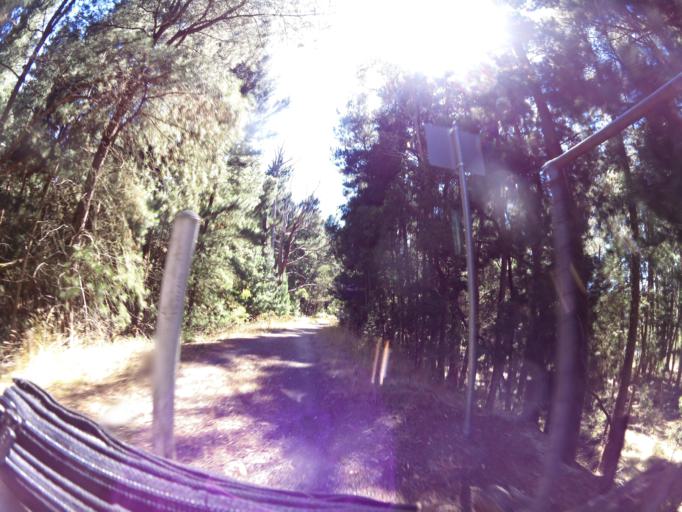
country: AU
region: Victoria
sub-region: Ballarat North
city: Delacombe
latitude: -37.6795
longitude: 143.5549
